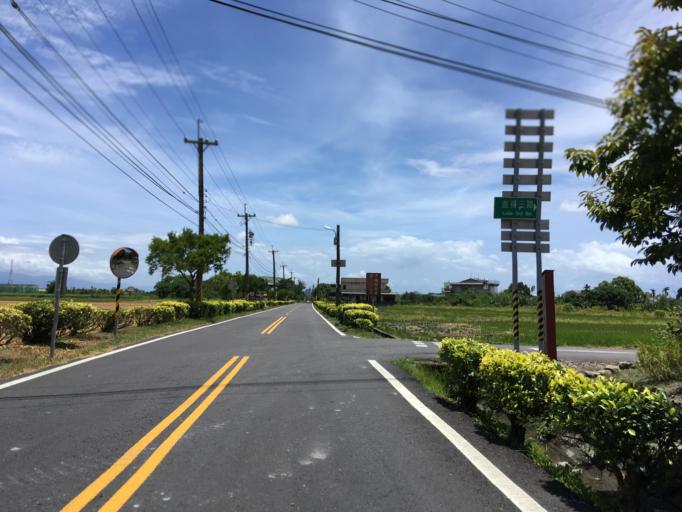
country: TW
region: Taiwan
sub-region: Yilan
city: Yilan
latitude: 24.6537
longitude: 121.7282
